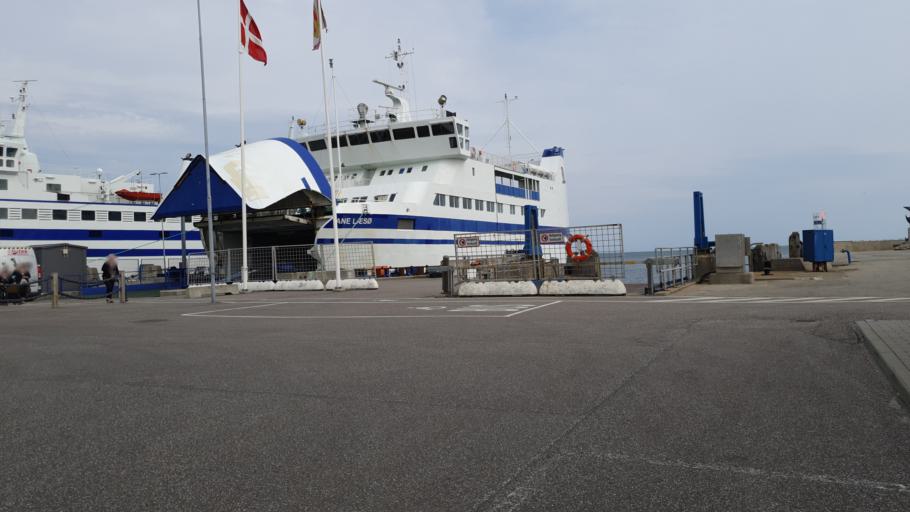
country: DK
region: North Denmark
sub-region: Laeso Kommune
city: Byrum
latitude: 57.2963
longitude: 10.9228
